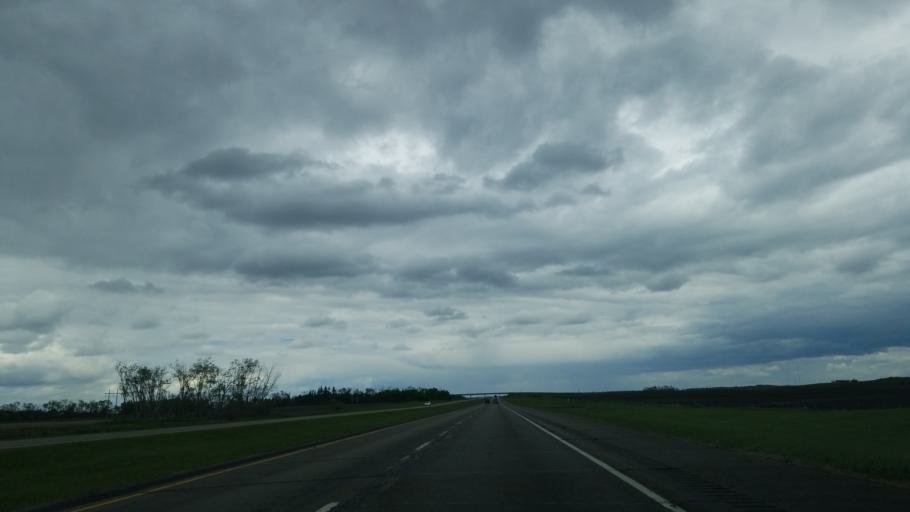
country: US
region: North Dakota
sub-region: Barnes County
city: Valley City
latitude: 46.9068
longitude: -98.2822
